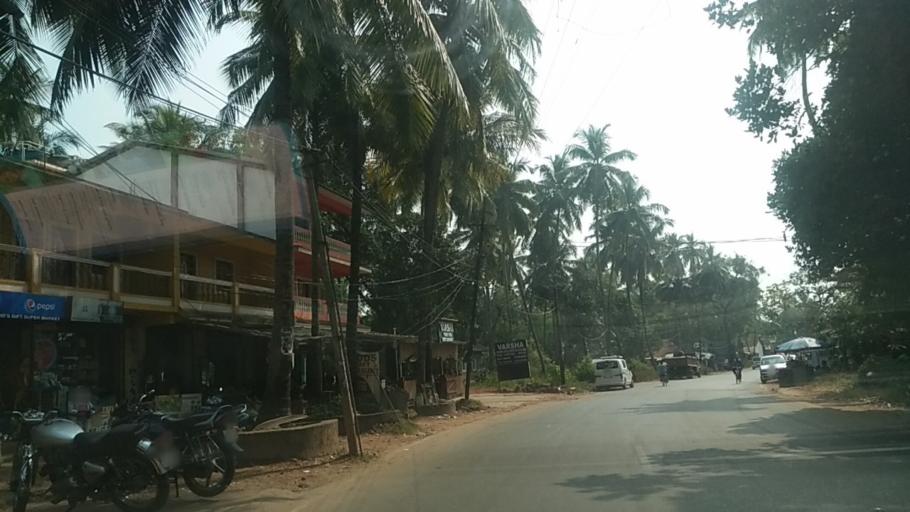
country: IN
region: Goa
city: Calangute
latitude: 15.5621
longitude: 73.7646
